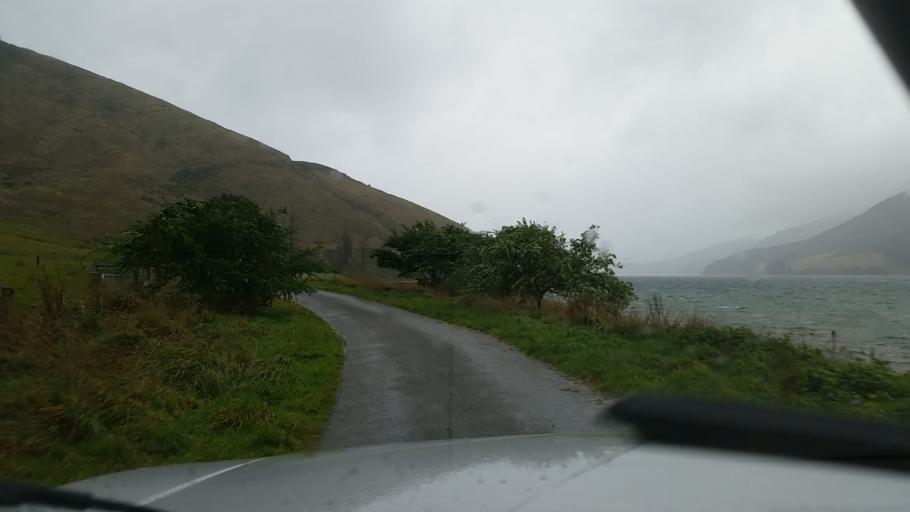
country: NZ
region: Marlborough
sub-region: Marlborough District
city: Picton
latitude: -41.1121
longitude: 174.0345
